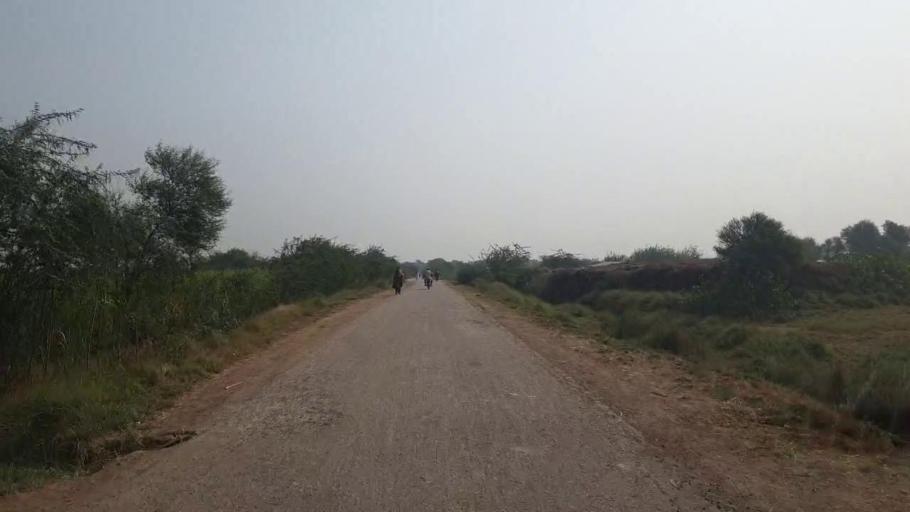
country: PK
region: Sindh
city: Tando Muhammad Khan
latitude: 25.2447
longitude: 68.5670
